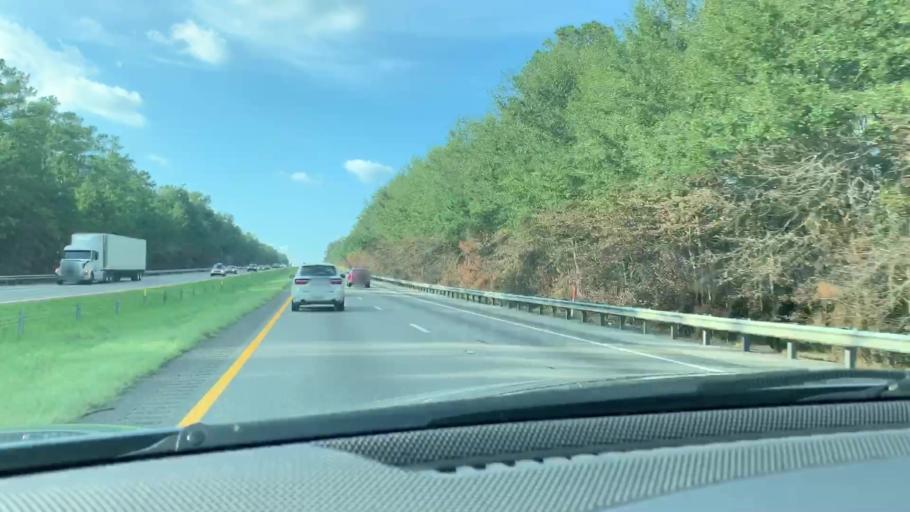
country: US
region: South Carolina
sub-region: Calhoun County
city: Oak Grove
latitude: 33.7226
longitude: -80.9270
